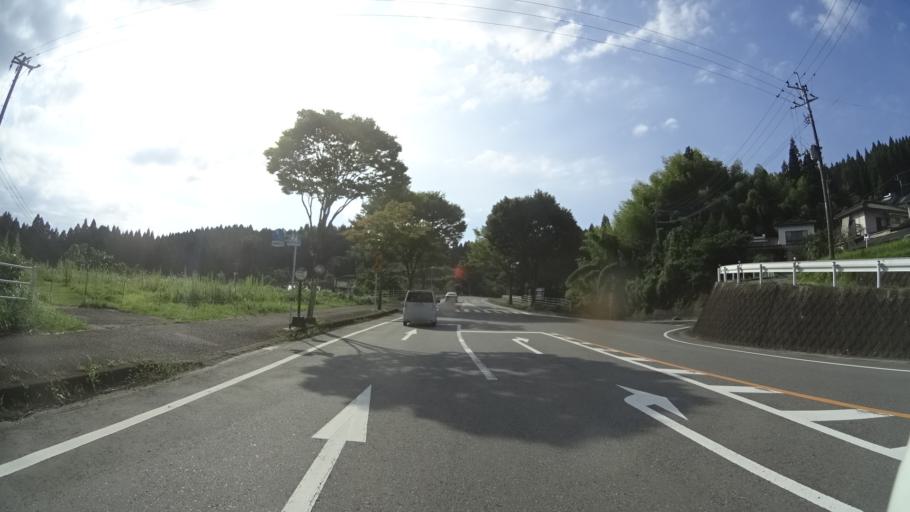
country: JP
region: Kumamoto
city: Ozu
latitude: 32.6878
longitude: 131.0024
